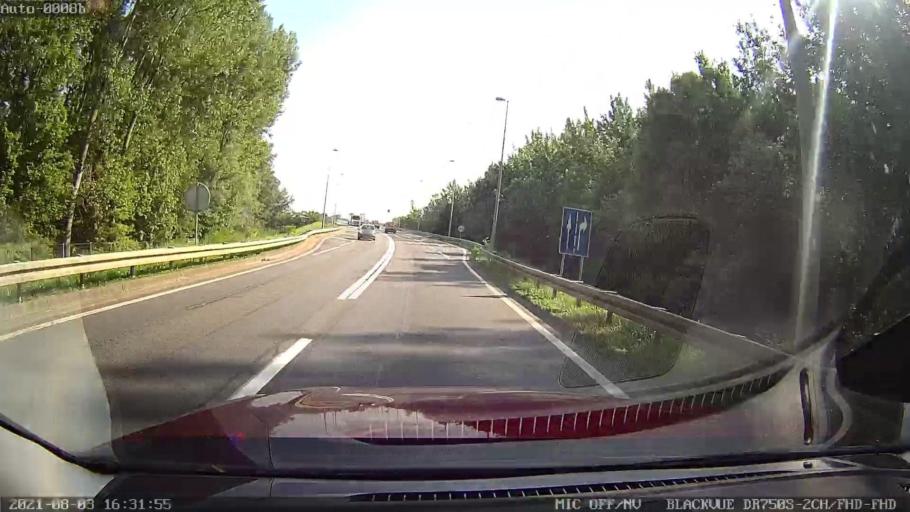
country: HR
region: Osjecko-Baranjska
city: Visnjevac
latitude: 45.5685
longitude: 18.6316
